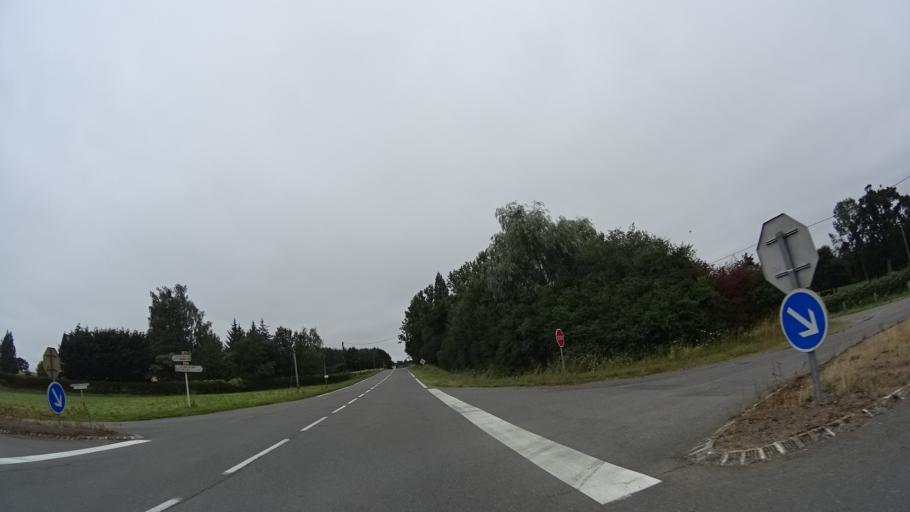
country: FR
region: Brittany
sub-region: Departement d'Ille-et-Vilaine
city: Vignoc
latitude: 48.2512
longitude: -1.8279
